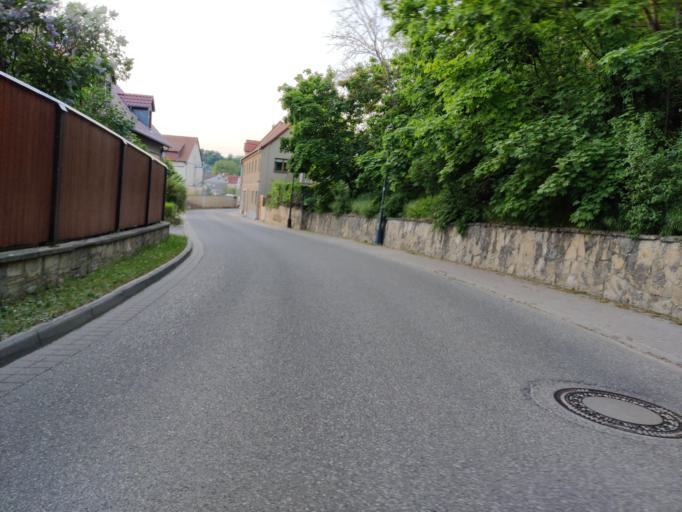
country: DE
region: Saxony-Anhalt
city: Freyburg
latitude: 51.2076
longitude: 11.7728
